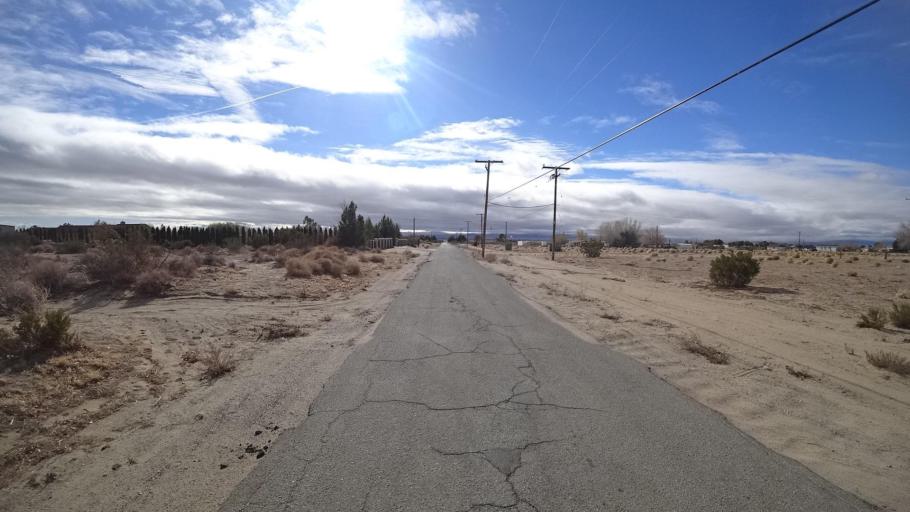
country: US
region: California
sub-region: Kern County
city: Rosamond
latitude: 34.8691
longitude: -118.2202
